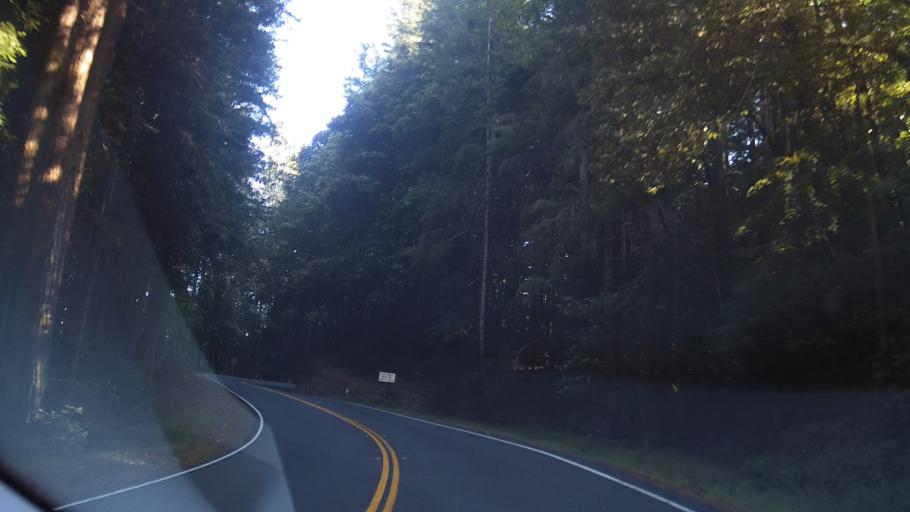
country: US
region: California
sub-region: Mendocino County
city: Fort Bragg
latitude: 39.3572
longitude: -123.6278
